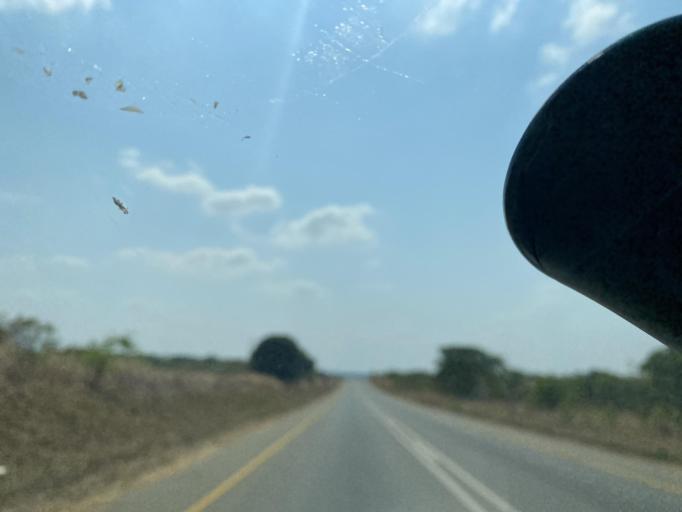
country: ZM
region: Lusaka
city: Chongwe
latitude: -15.5303
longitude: 28.6287
